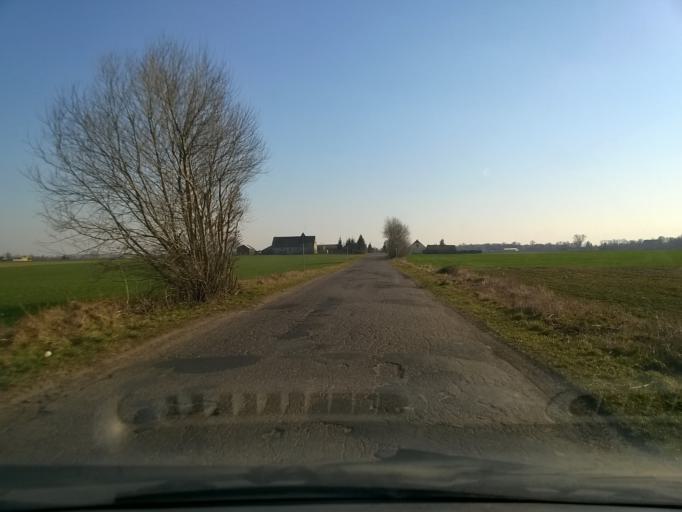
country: PL
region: Greater Poland Voivodeship
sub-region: Powiat wagrowiecki
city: Golancz
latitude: 52.9720
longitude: 17.3360
